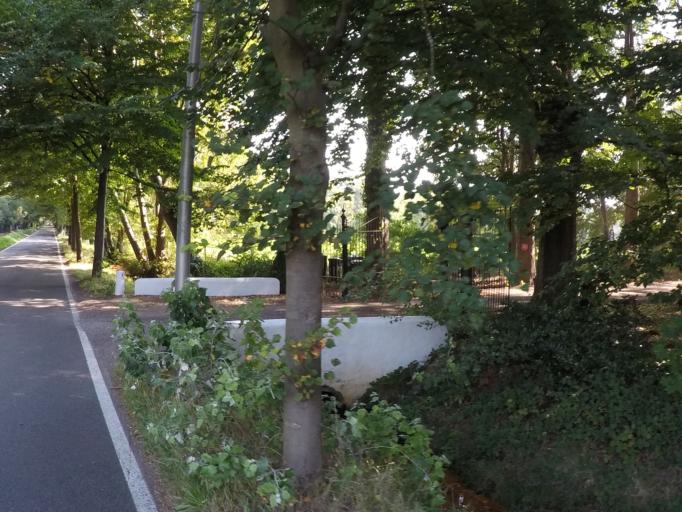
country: BE
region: Flanders
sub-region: Provincie Antwerpen
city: Kapellen
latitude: 51.3229
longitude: 4.4088
